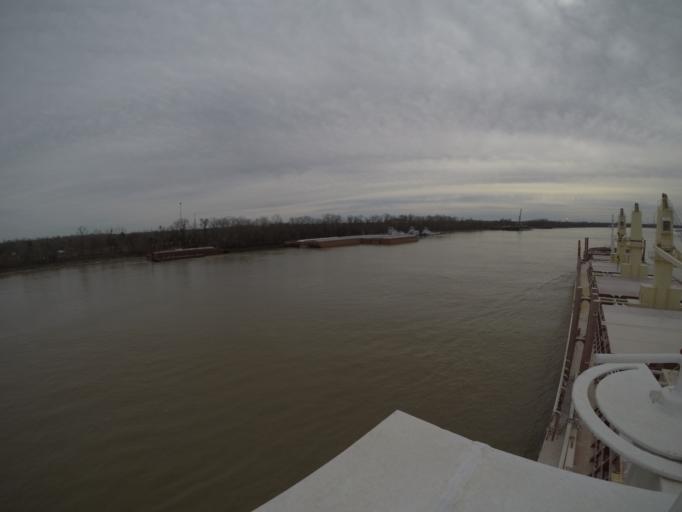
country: US
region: Louisiana
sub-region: Saint John the Baptist Parish
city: Laplace
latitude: 30.0445
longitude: -90.4756
